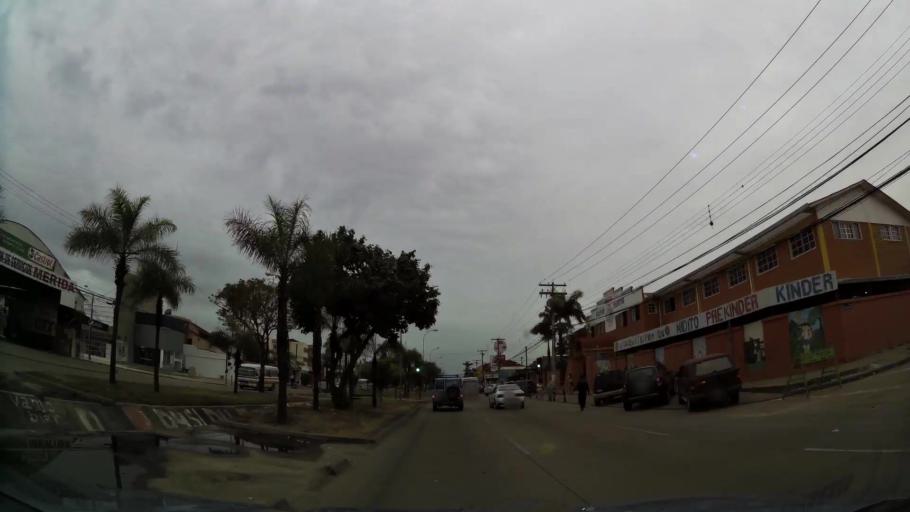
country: BO
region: Santa Cruz
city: Santa Cruz de la Sierra
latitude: -17.8172
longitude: -63.1836
